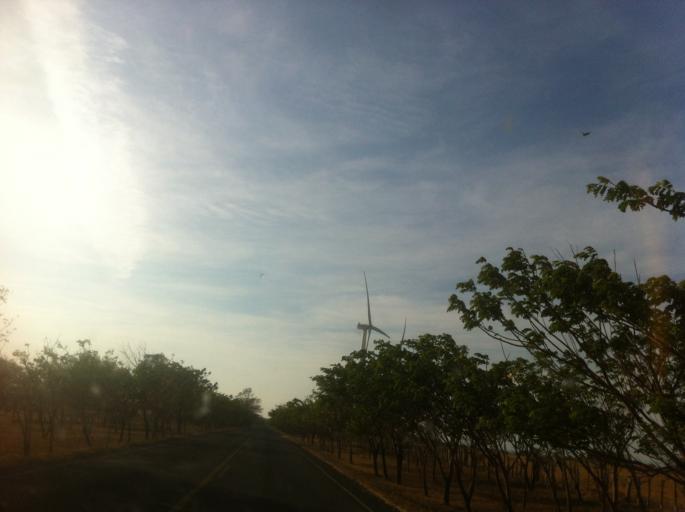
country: NI
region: Rivas
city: San Jorge
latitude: 11.3128
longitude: -85.7049
